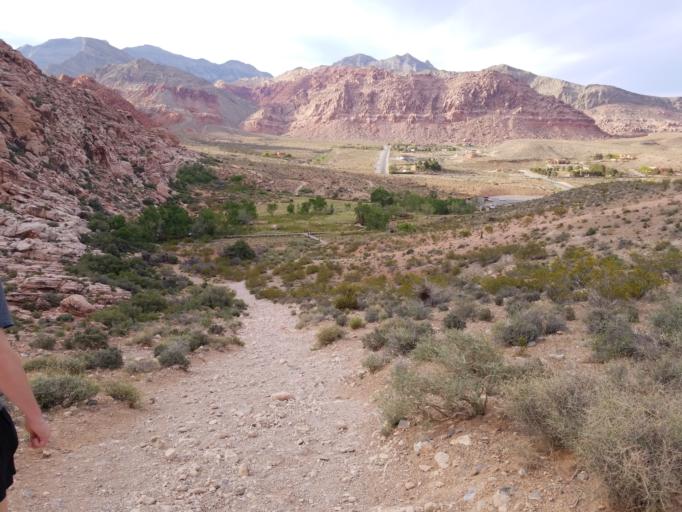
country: US
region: Nevada
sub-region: Clark County
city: Summerlin South
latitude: 36.1431
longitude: -115.4196
